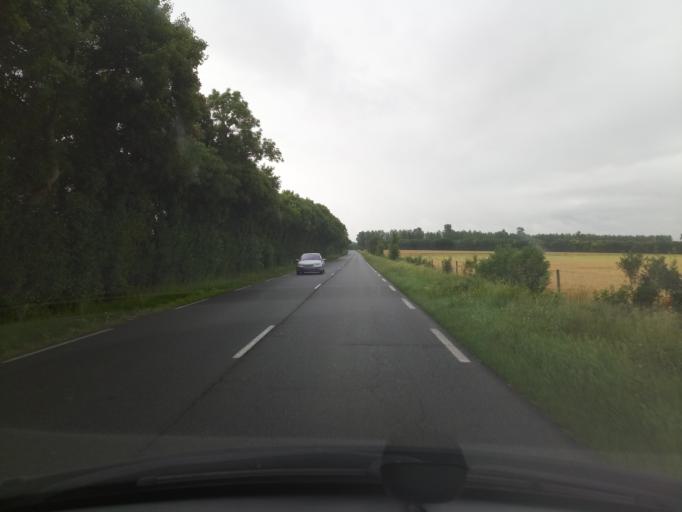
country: FR
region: Poitou-Charentes
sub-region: Departement de la Charente-Maritime
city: Courcon
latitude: 46.1717
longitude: -0.8407
